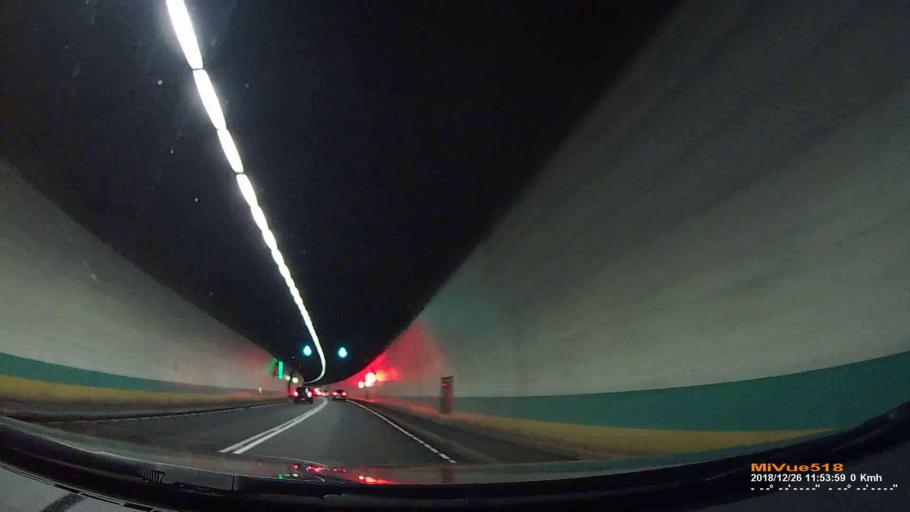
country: TW
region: Taiwan
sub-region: Keelung
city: Keelung
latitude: 24.9540
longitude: 121.6968
